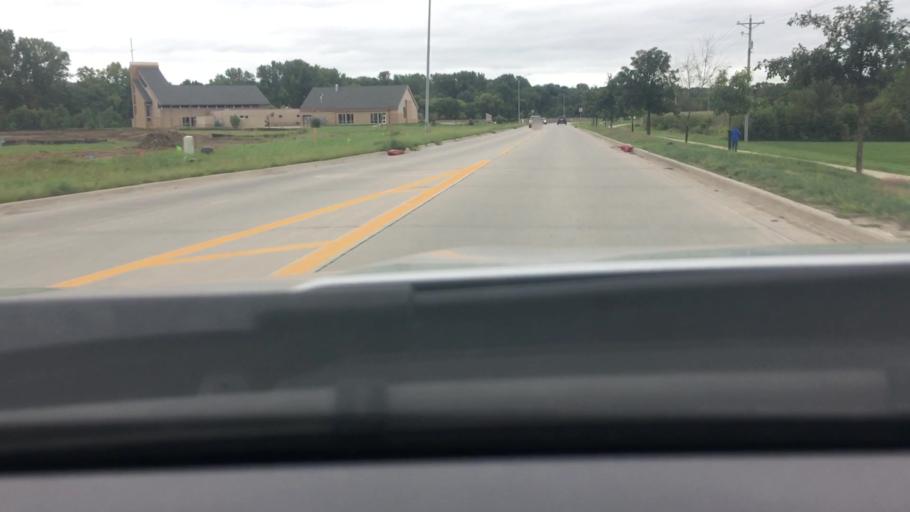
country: US
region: Iowa
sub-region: Pottawattamie County
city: Council Bluffs
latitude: 41.2665
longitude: -95.8039
